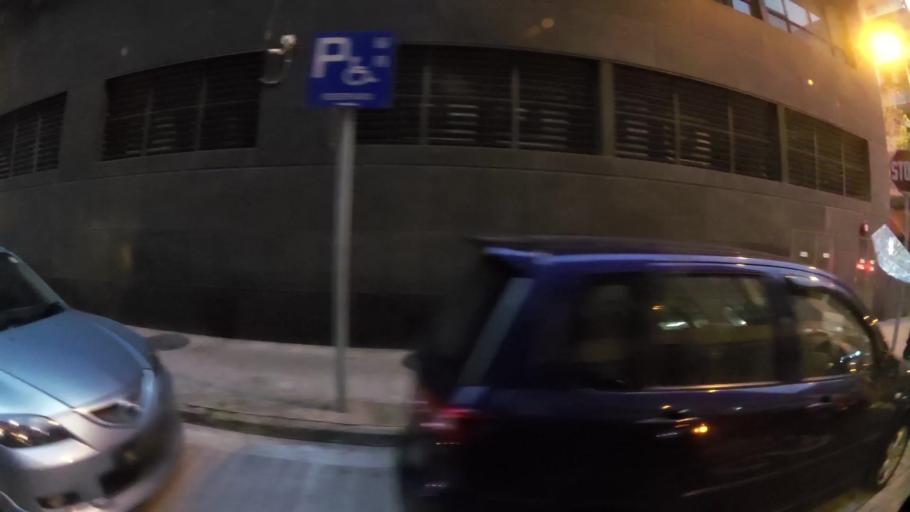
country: MO
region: Macau
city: Macau
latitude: 22.2059
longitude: 113.5460
